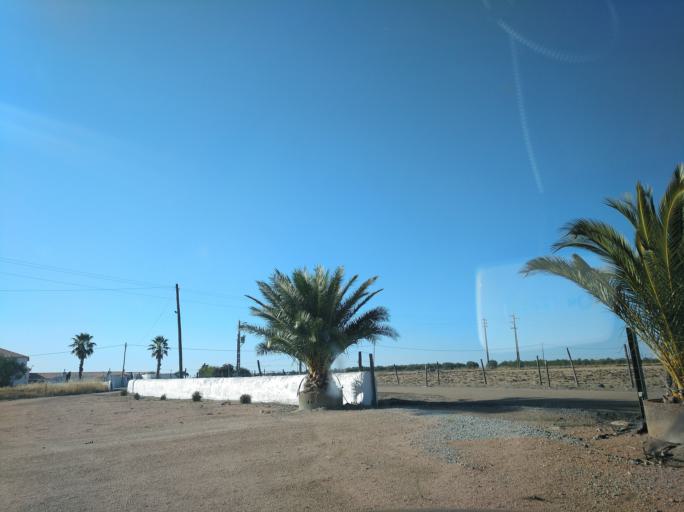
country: PT
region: Portalegre
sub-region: Elvas
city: Elvas
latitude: 38.9459
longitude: -7.1883
